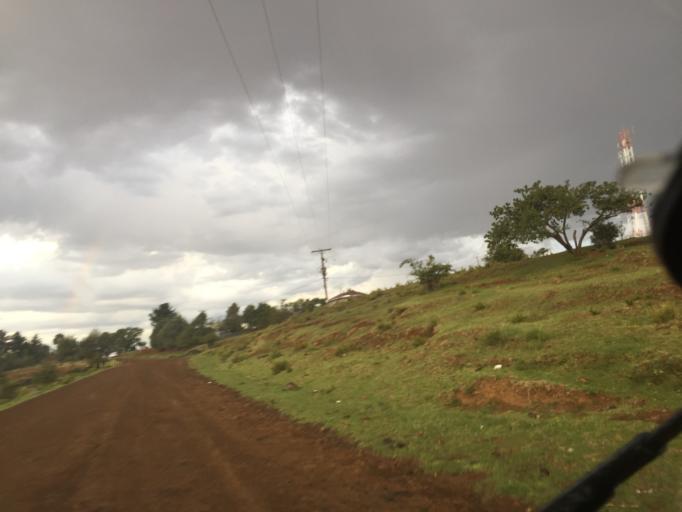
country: LS
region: Berea
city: Teyateyaneng
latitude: -29.1577
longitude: 28.0344
